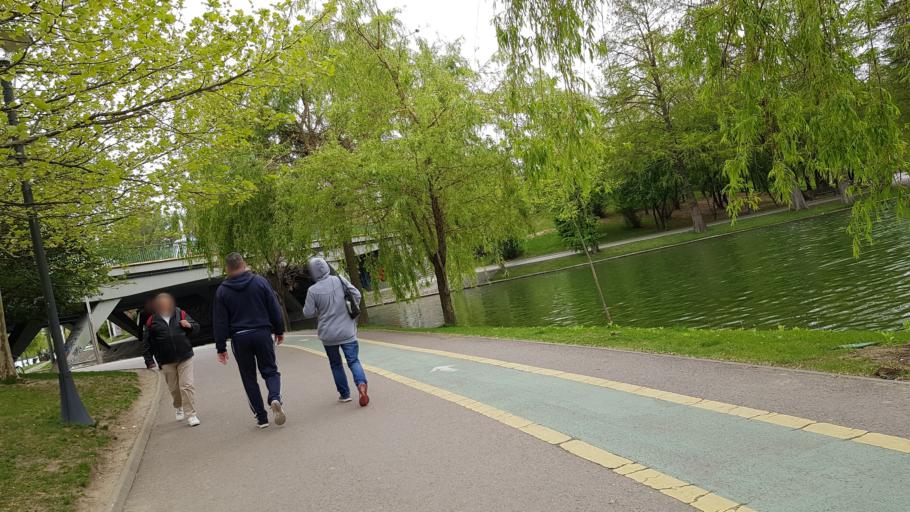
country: RO
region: Ilfov
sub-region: Comuna Fundeni-Dobroesti
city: Fundeni
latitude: 44.4244
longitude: 26.1562
